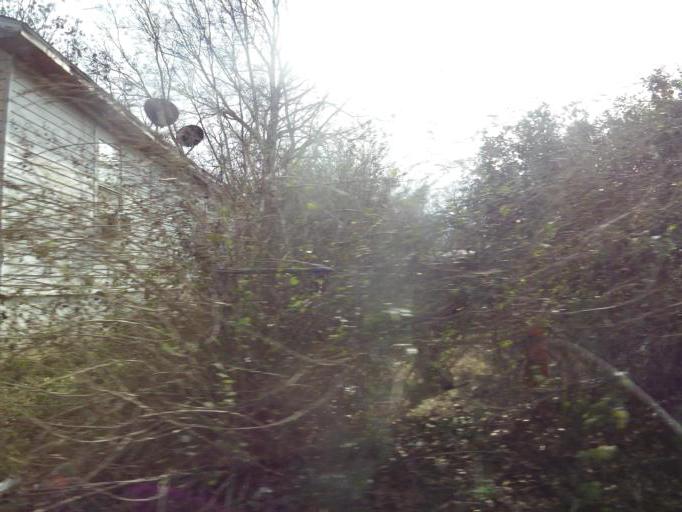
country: US
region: Alabama
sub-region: Houston County
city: Dothan
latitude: 31.2265
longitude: -85.3787
